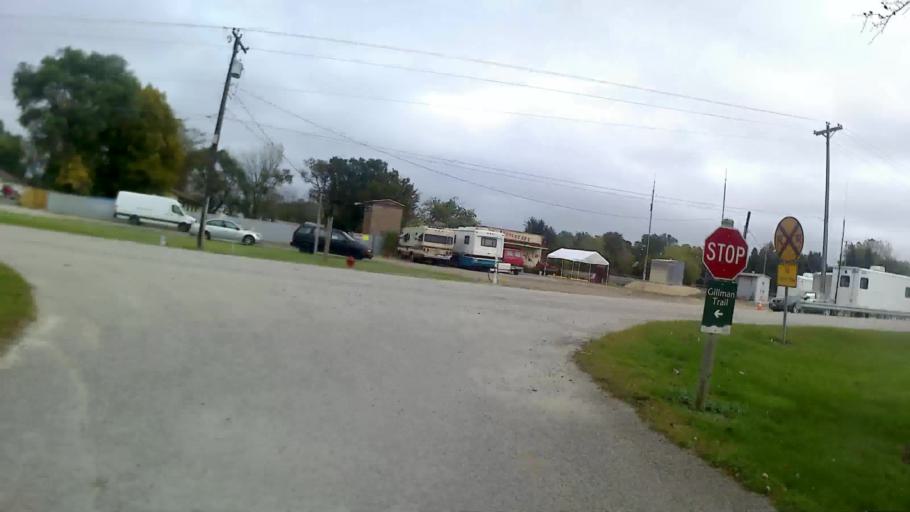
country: US
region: Illinois
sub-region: Kane County
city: Montgomery
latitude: 41.7461
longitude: -88.3448
